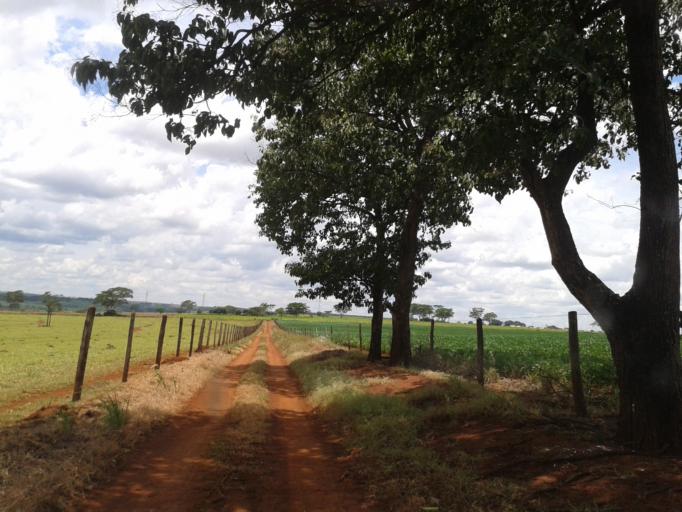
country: BR
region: Minas Gerais
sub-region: Centralina
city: Centralina
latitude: -18.7123
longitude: -49.2188
